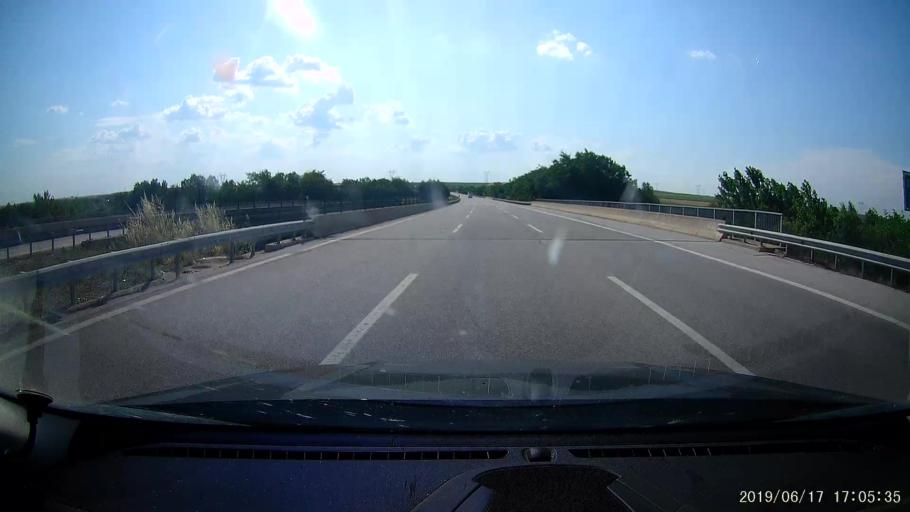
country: TR
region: Edirne
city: Edirne
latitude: 41.6608
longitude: 26.6952
